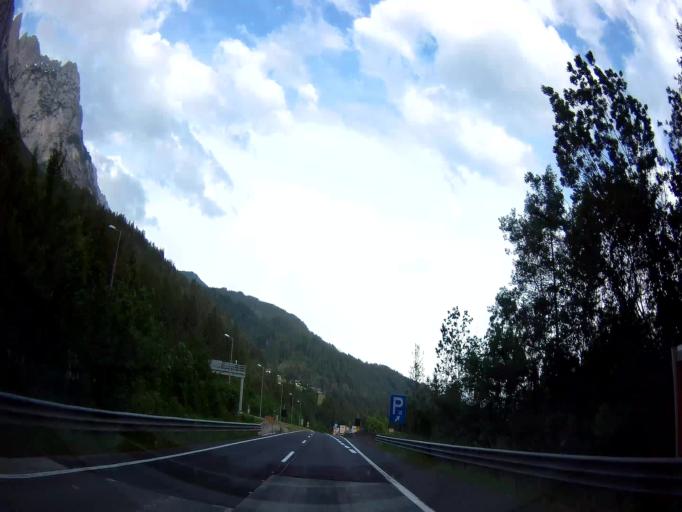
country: AT
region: Salzburg
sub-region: Politischer Bezirk Sankt Johann im Pongau
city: Werfen
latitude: 47.4921
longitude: 13.1828
